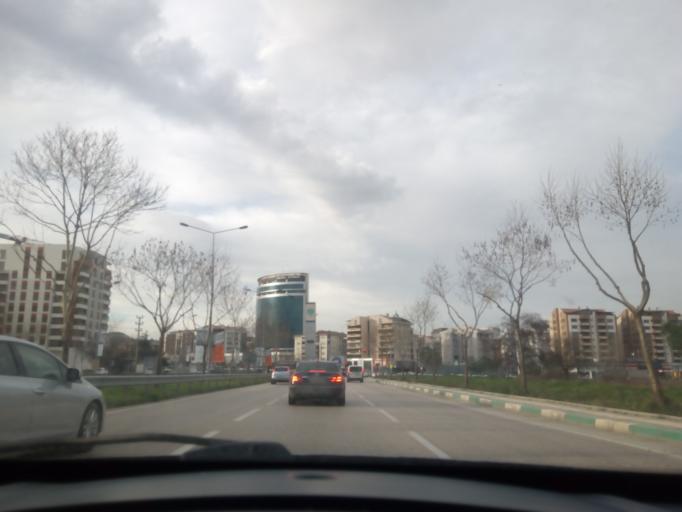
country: TR
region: Bursa
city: Cali
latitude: 40.2216
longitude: 28.9543
